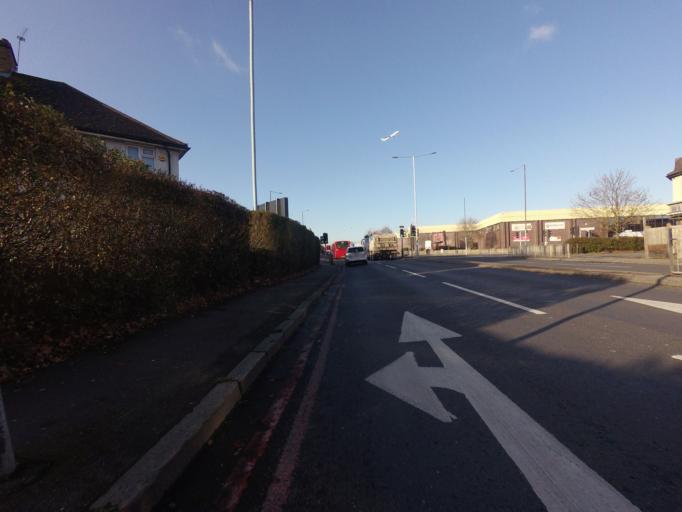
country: GB
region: England
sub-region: Greater London
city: Feltham
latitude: 51.4569
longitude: -0.4100
